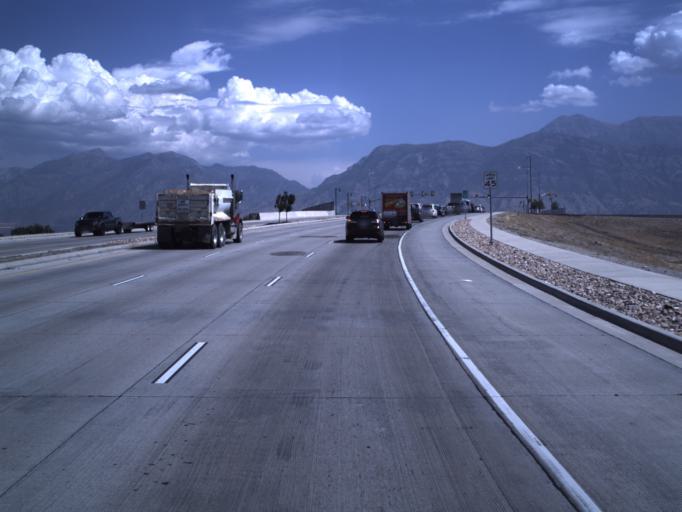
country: US
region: Utah
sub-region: Utah County
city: Lehi
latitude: 40.3764
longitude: -111.8351
